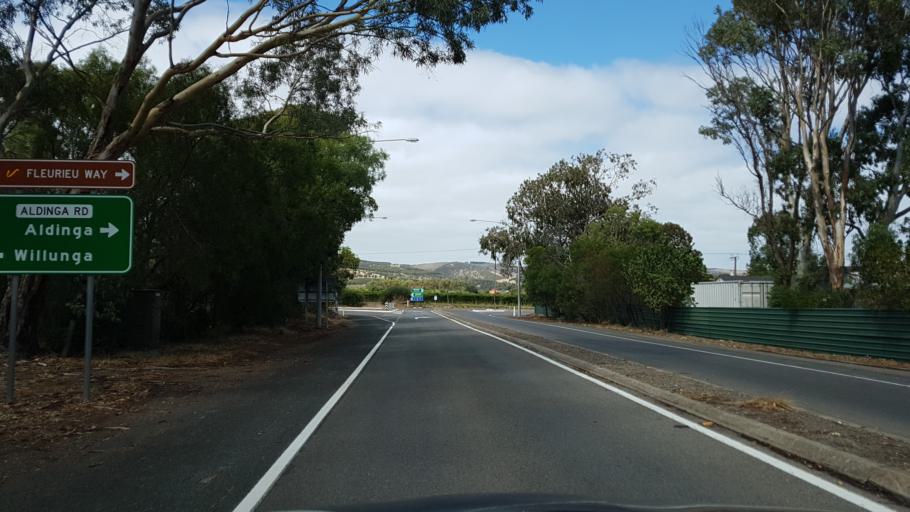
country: AU
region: South Australia
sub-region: Onkaparinga
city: McLaren Vale
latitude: -35.2713
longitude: 138.5368
